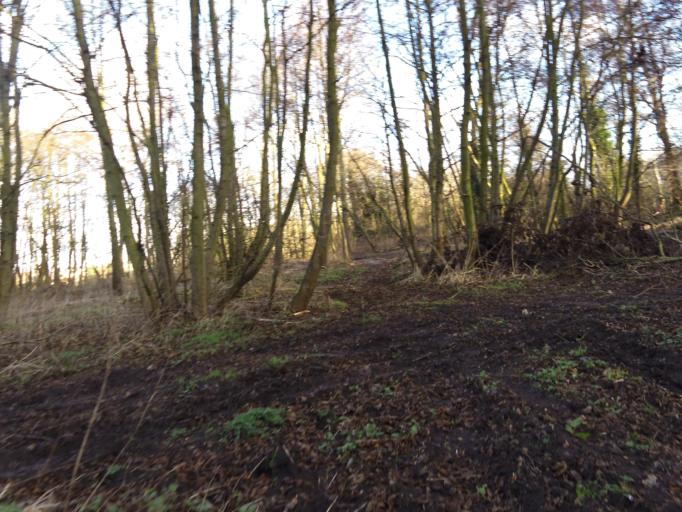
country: NL
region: South Holland
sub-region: Gemeente Noordwijkerhout
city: Noordwijkerhout
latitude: 52.2685
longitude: 4.4880
